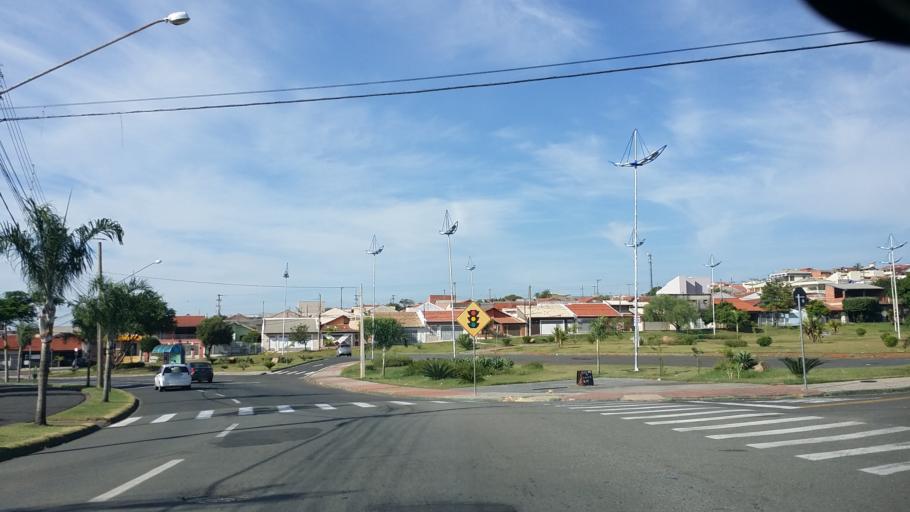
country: BR
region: Sao Paulo
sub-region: Indaiatuba
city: Indaiatuba
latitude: -23.1022
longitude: -47.2296
